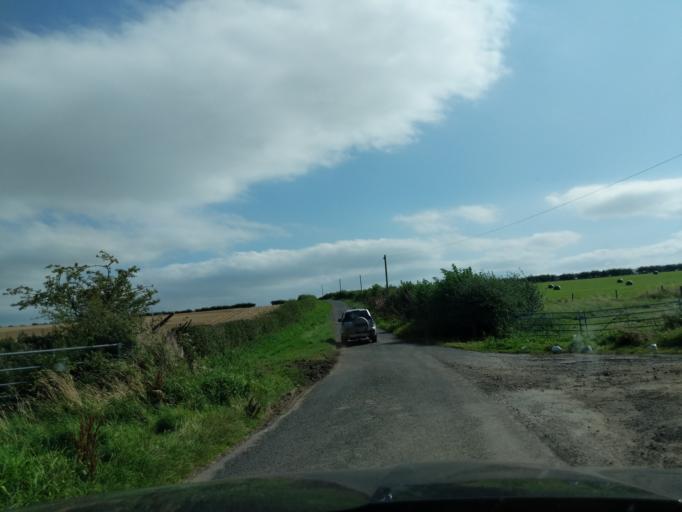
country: GB
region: England
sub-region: Northumberland
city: Ford
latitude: 55.6556
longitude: -2.1494
